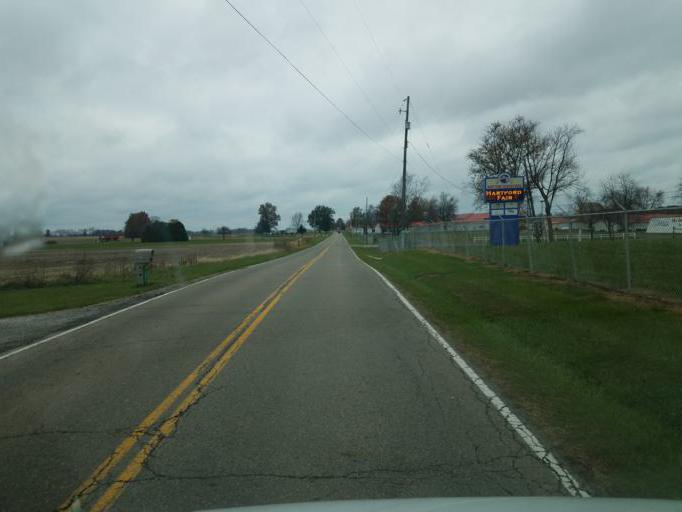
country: US
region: Ohio
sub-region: Knox County
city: Centerburg
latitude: 40.2469
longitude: -82.6828
